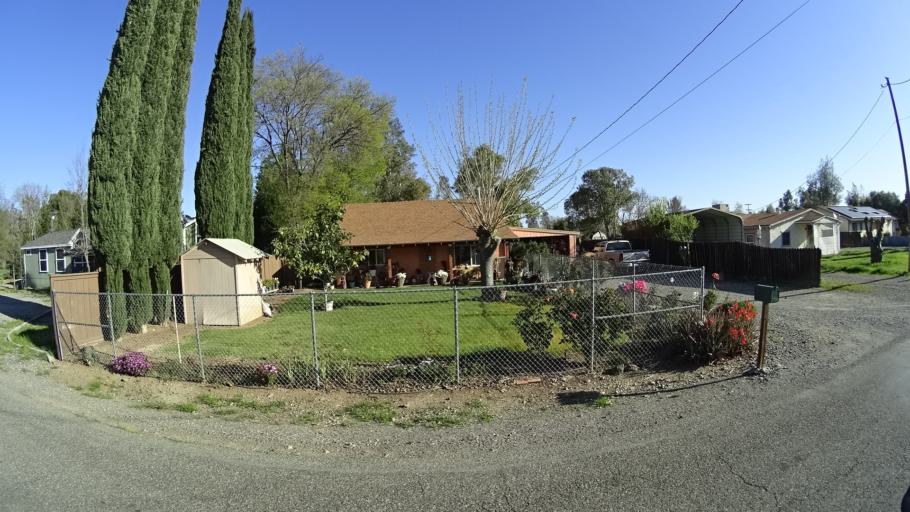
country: US
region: California
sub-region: Glenn County
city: Orland
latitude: 39.7549
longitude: -122.2284
